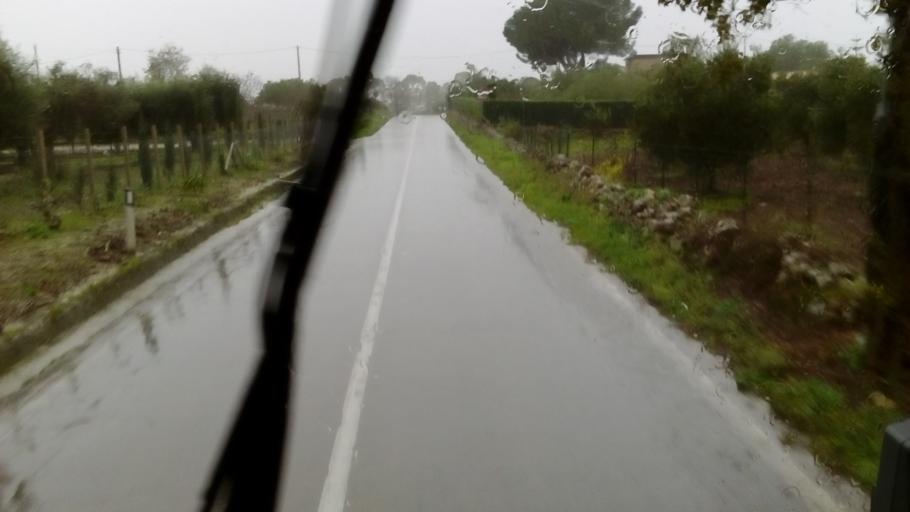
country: IT
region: Sicily
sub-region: Enna
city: Pietraperzia
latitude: 37.4209
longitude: 14.1598
